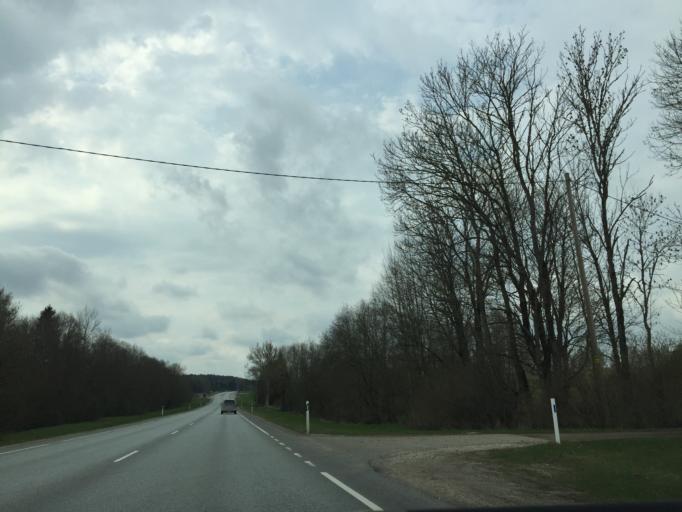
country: EE
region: Tartu
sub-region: Noo vald
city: Noo
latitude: 58.2625
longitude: 26.4811
